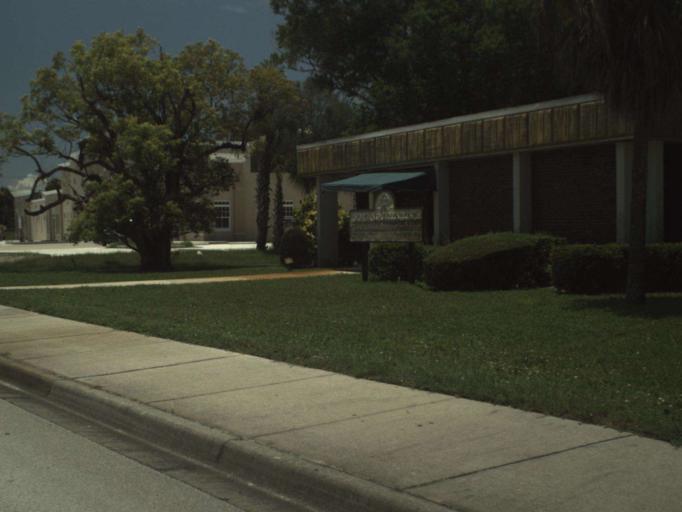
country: US
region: Florida
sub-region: Indian River County
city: Winter Beach
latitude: 27.7534
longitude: -80.4367
